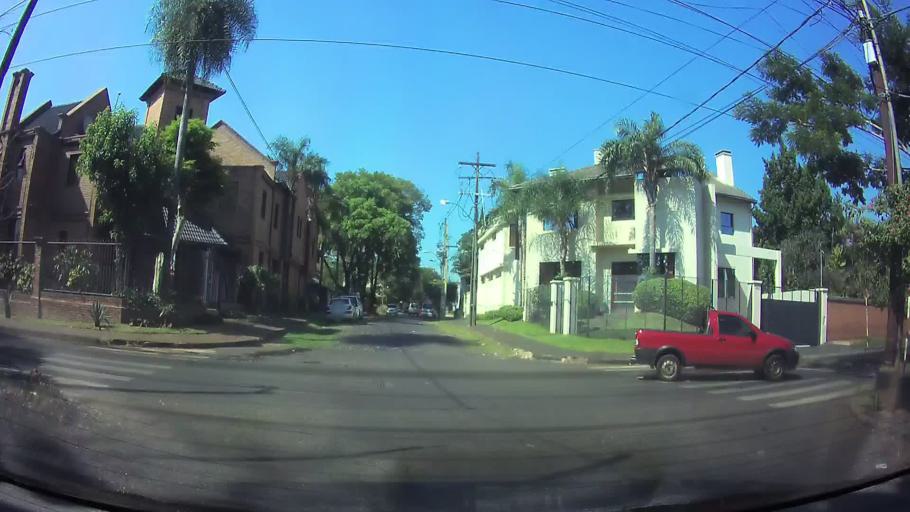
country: PY
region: Central
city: Fernando de la Mora
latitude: -25.2909
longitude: -57.5640
